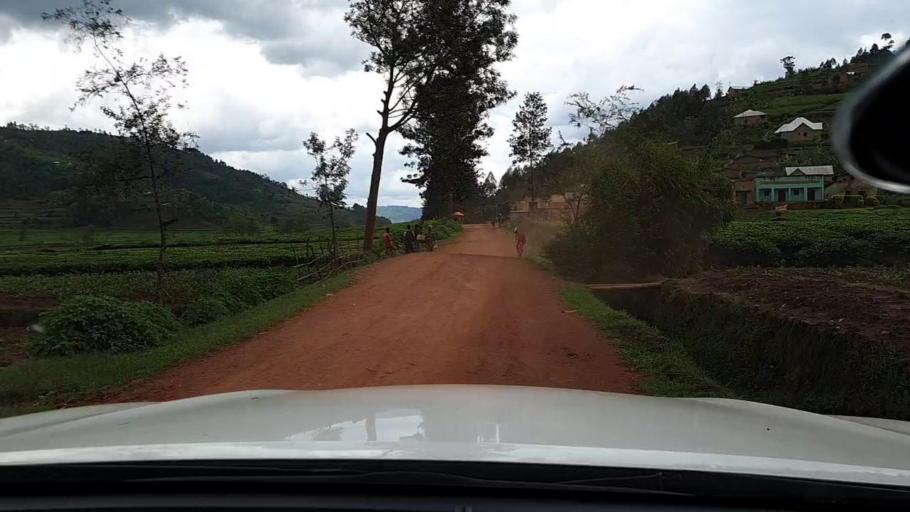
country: RW
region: Northern Province
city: Byumba
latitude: -1.6697
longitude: 29.9256
